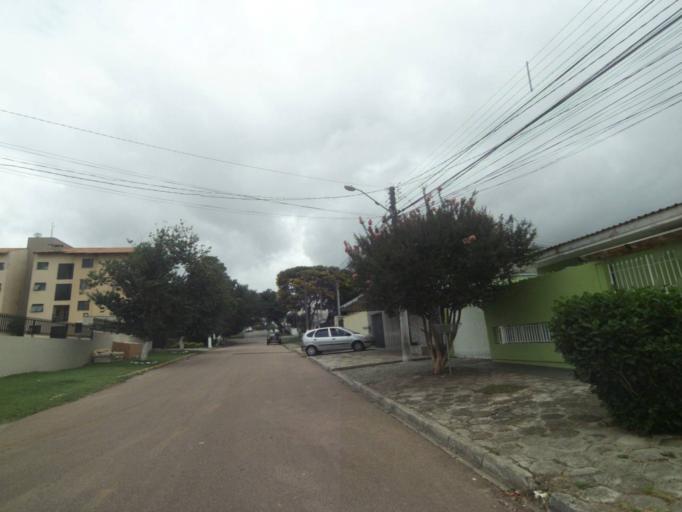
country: BR
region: Parana
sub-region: Curitiba
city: Curitiba
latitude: -25.4918
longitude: -49.3057
